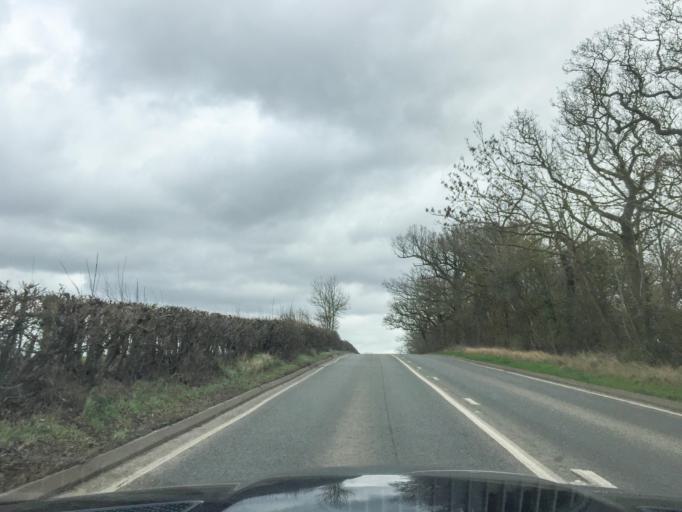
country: GB
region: England
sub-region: Warwickshire
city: Wellesbourne Mountford
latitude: 52.1255
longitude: -1.5634
